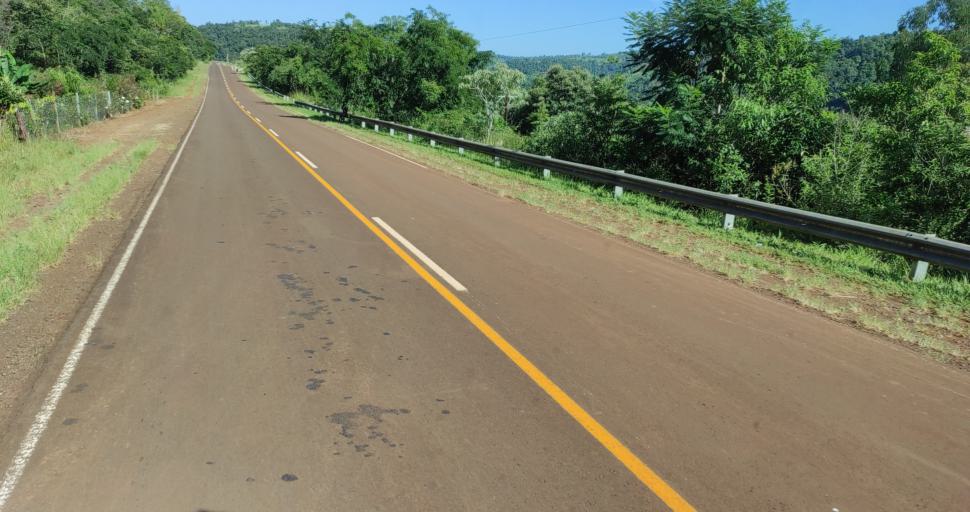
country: AR
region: Misiones
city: El Soberbio
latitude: -27.2246
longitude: -54.0635
